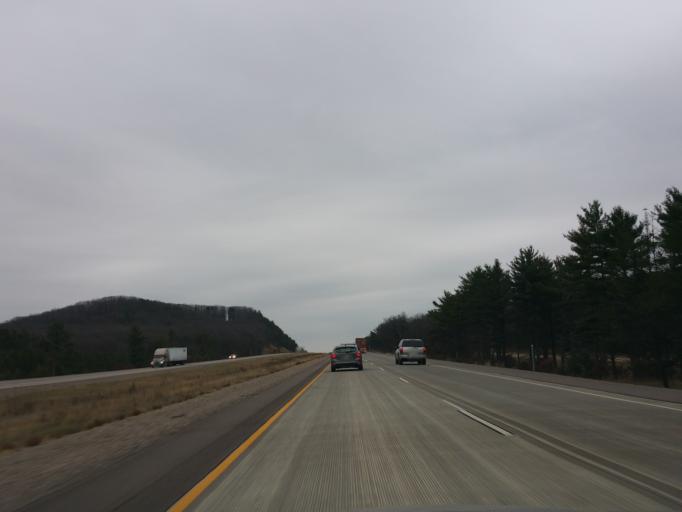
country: US
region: Wisconsin
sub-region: Jackson County
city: Black River Falls
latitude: 44.3430
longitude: -90.9183
